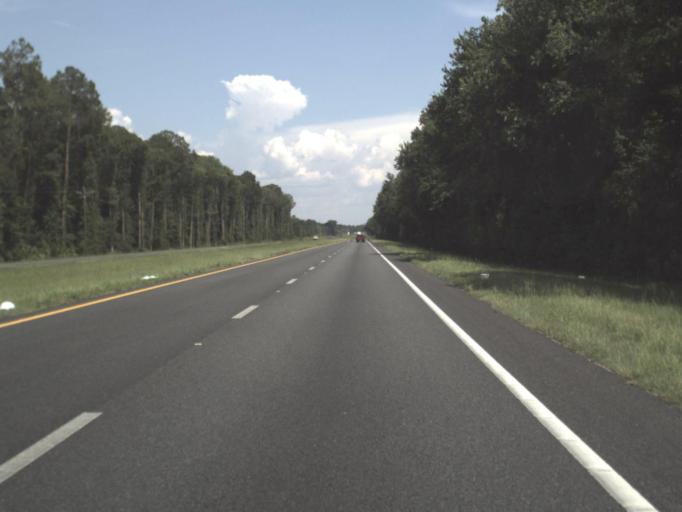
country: US
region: Florida
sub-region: Alachua County
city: Waldo
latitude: 29.7736
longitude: -82.1579
